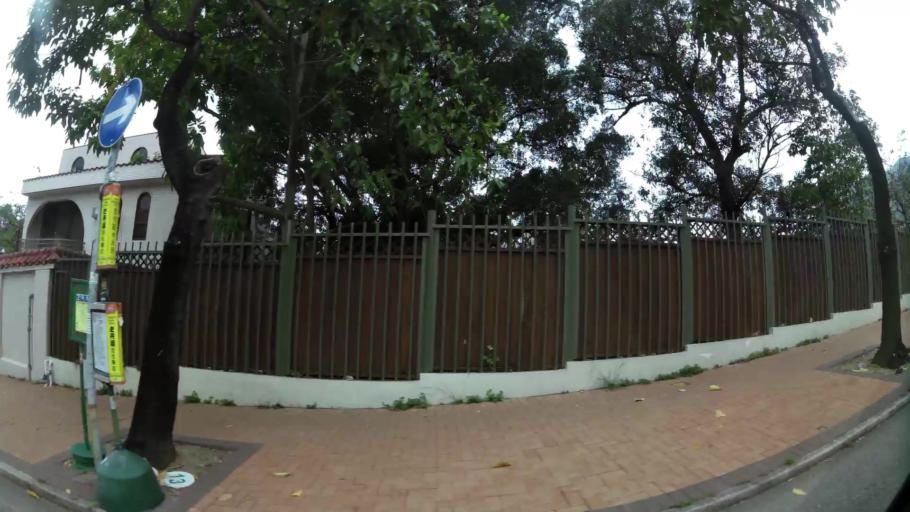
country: HK
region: Wong Tai Sin
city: Wong Tai Sin
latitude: 22.3413
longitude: 114.1807
